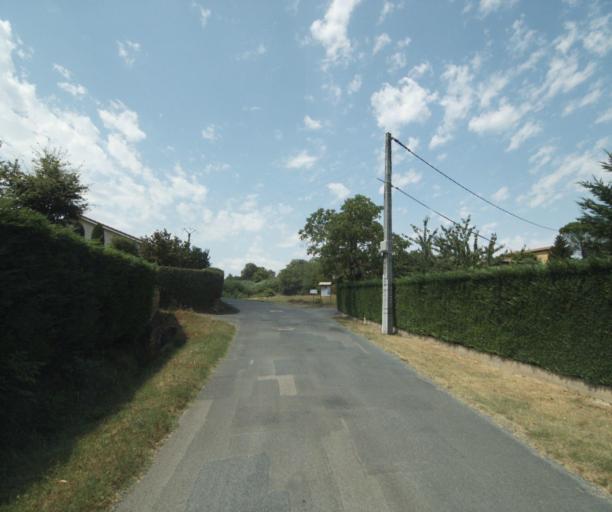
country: FR
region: Rhone-Alpes
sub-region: Departement du Rhone
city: Saint-Germain-Nuelles
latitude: 45.8503
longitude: 4.6252
